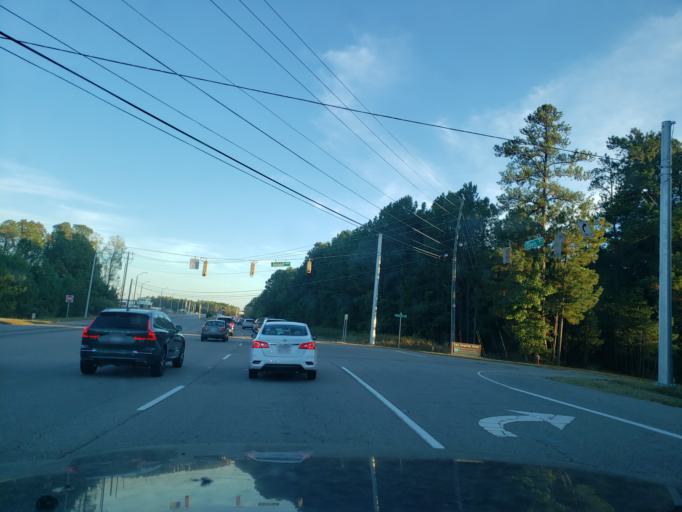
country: US
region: North Carolina
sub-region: Wake County
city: Morrisville
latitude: 35.8290
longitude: -78.8527
